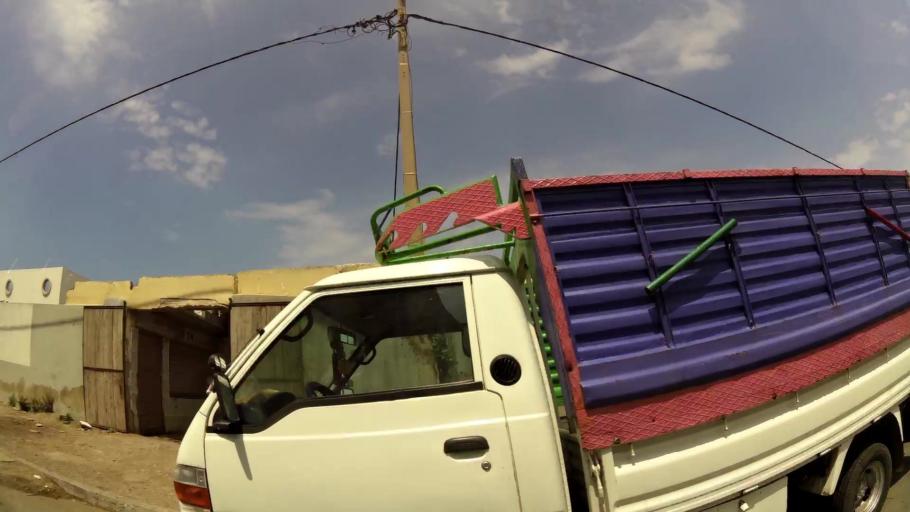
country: MA
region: Rabat-Sale-Zemmour-Zaer
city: Sale
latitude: 34.0554
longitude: -6.8201
